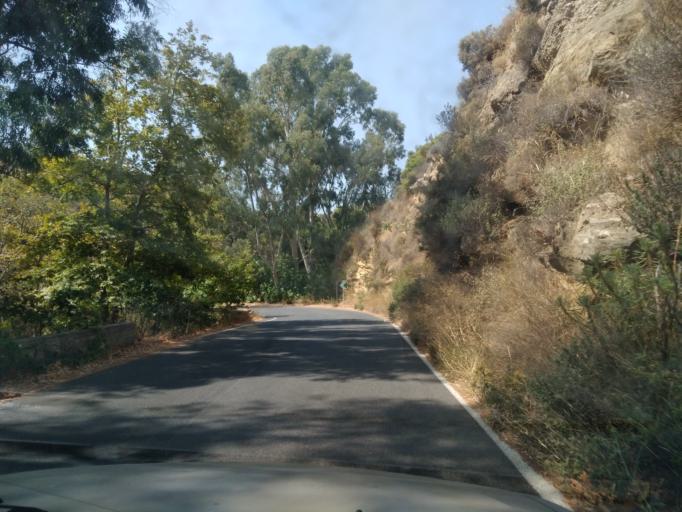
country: GR
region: Crete
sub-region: Nomos Lasithiou
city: Siteia
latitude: 35.1407
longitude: 26.0735
